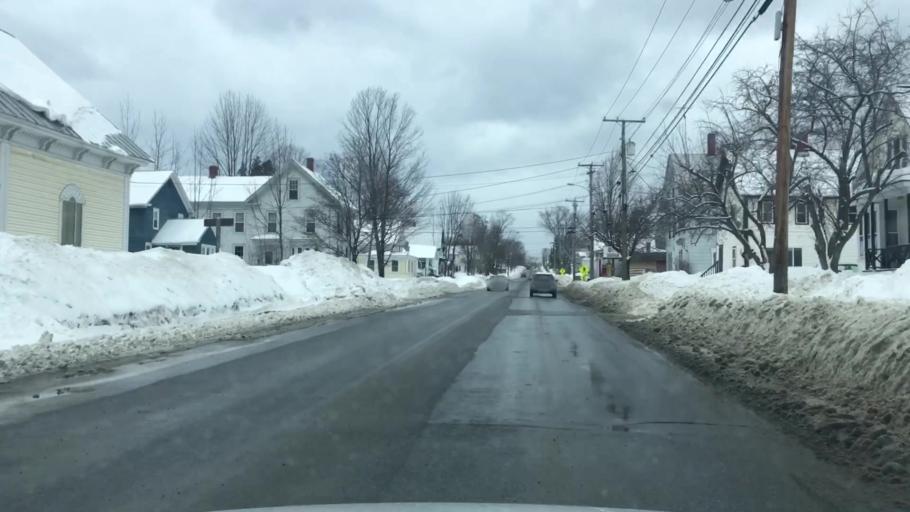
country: US
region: Maine
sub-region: Somerset County
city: Skowhegan
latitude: 44.7696
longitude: -69.7170
